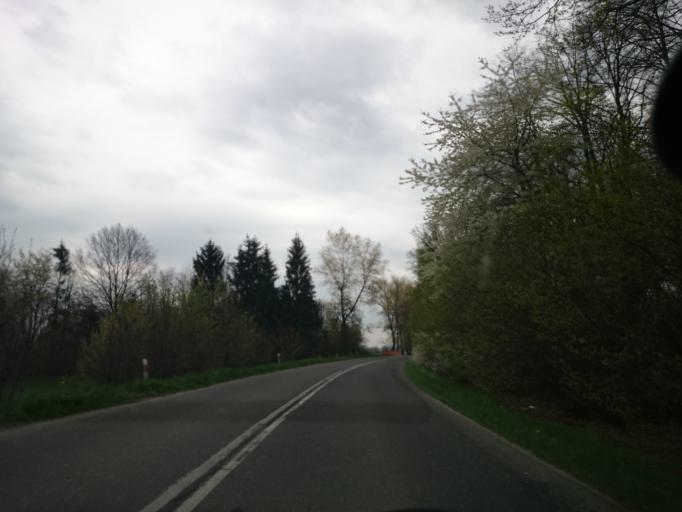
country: PL
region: Opole Voivodeship
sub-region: Powiat nyski
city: Glucholazy
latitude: 50.3638
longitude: 17.3733
